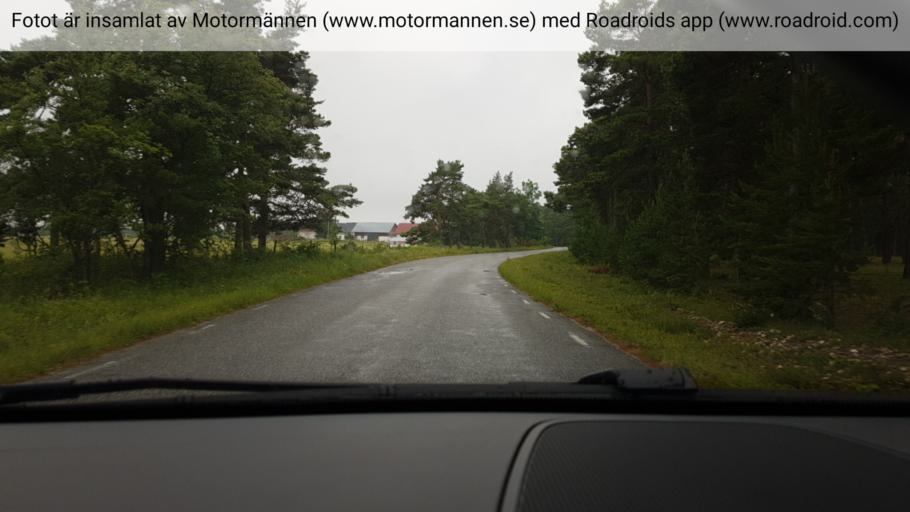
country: SE
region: Gotland
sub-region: Gotland
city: Slite
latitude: 57.8678
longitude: 18.8702
